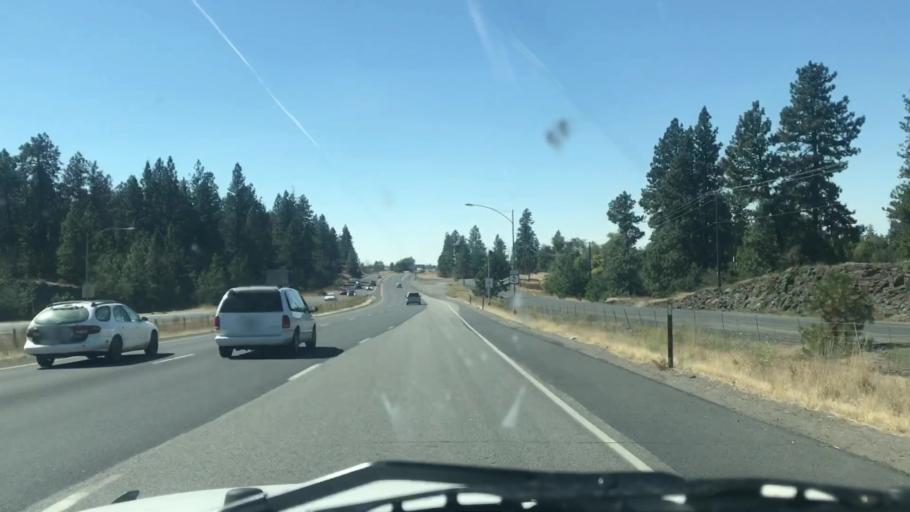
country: US
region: Washington
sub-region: Spokane County
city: Spokane
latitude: 47.6433
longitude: -117.5052
